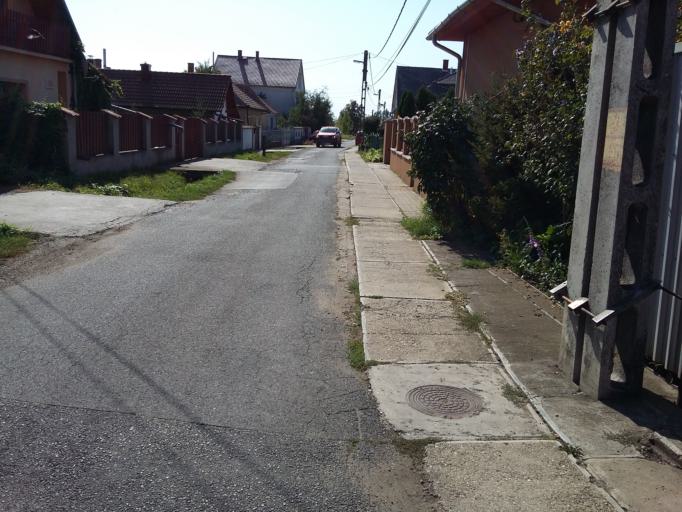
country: HU
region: Borsod-Abauj-Zemplen
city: Bekecs
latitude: 48.1509
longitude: 21.1733
